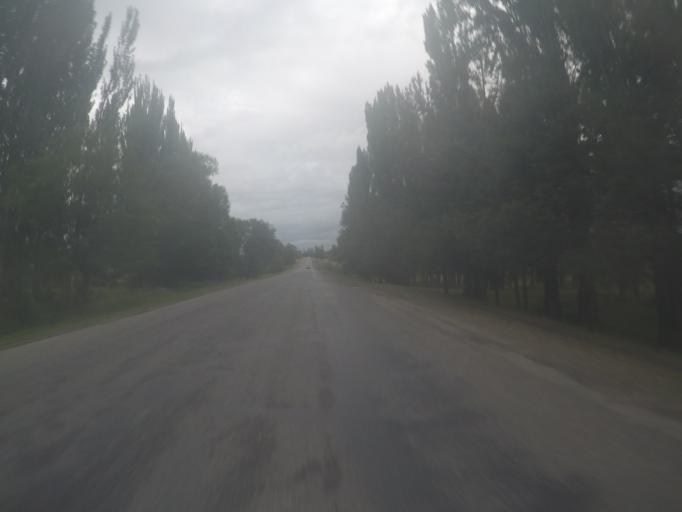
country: KG
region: Ysyk-Koel
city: Karakol
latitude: 42.5884
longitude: 78.3876
